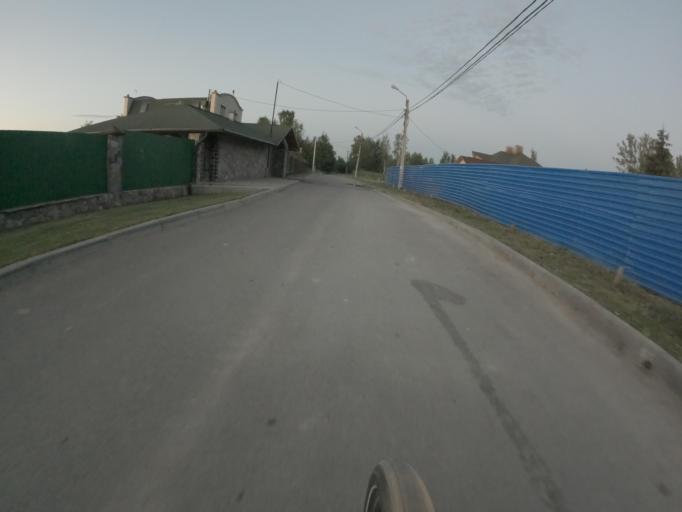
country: RU
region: St.-Petersburg
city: Sapernyy
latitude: 59.7826
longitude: 30.6788
